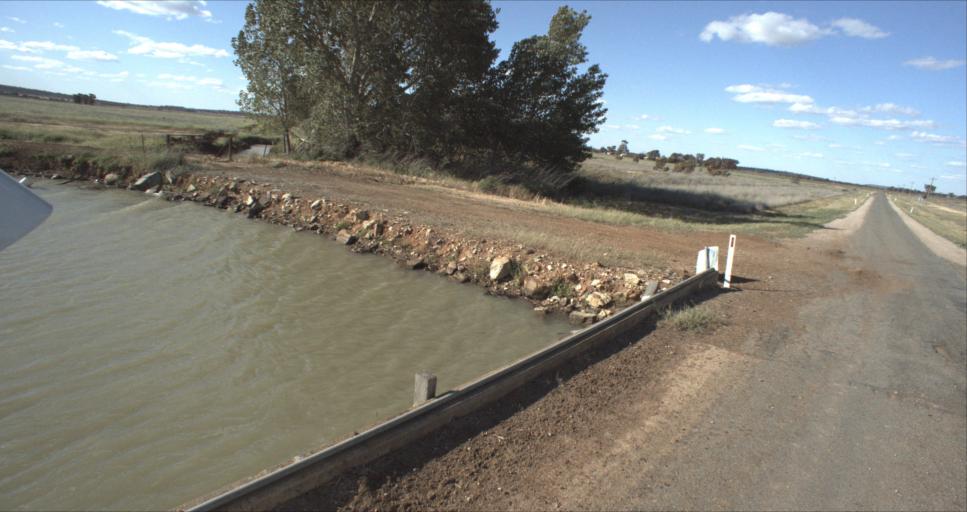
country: AU
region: New South Wales
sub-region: Leeton
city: Leeton
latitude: -34.4582
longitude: 146.2701
